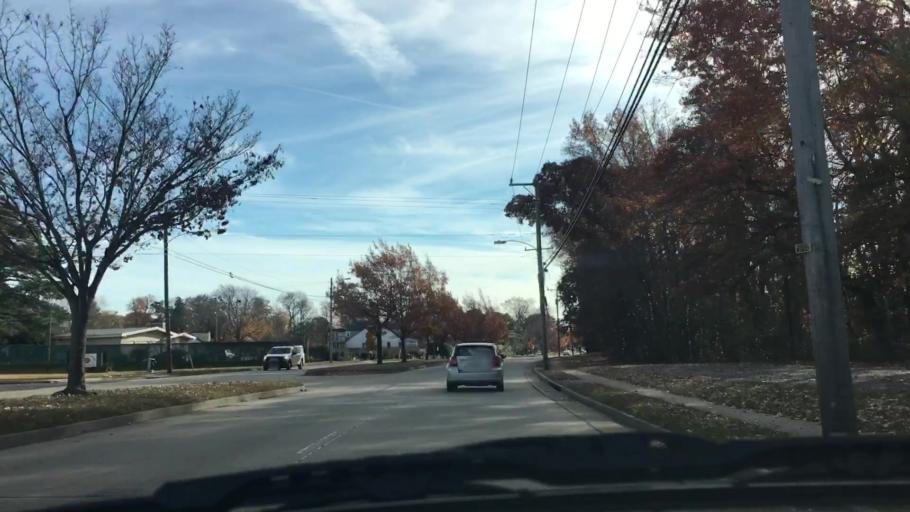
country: US
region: Virginia
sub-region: City of Norfolk
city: Norfolk
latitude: 36.9244
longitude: -76.2526
